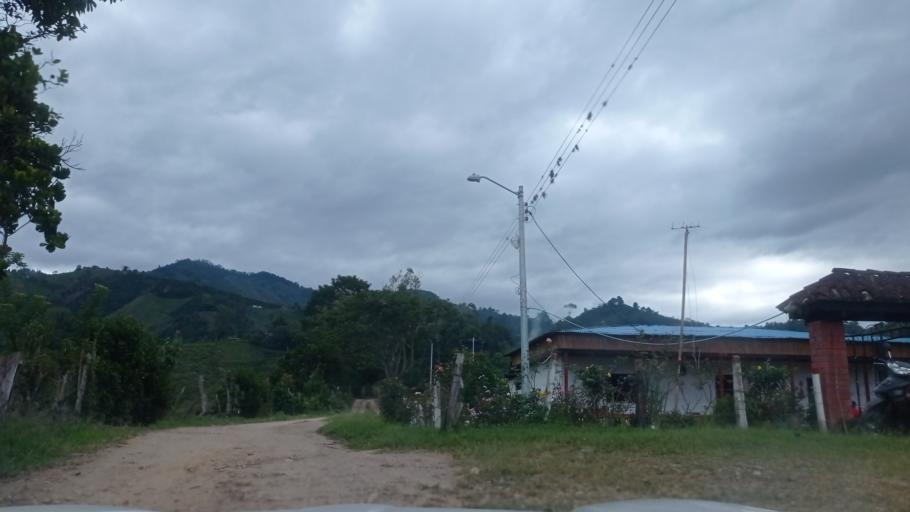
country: CO
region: Huila
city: Garzon
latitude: 2.1011
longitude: -75.6295
